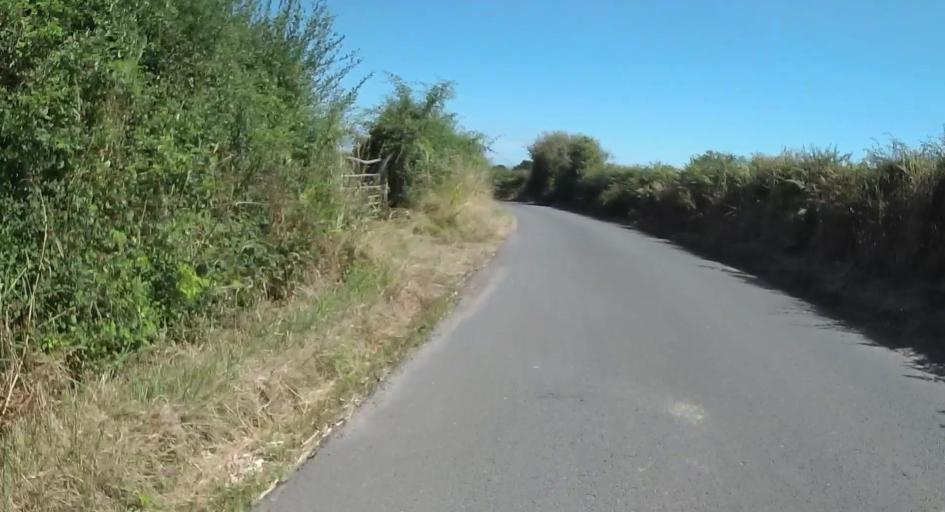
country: GB
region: England
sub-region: Dorset
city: Bovington Camp
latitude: 50.7378
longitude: -2.2176
